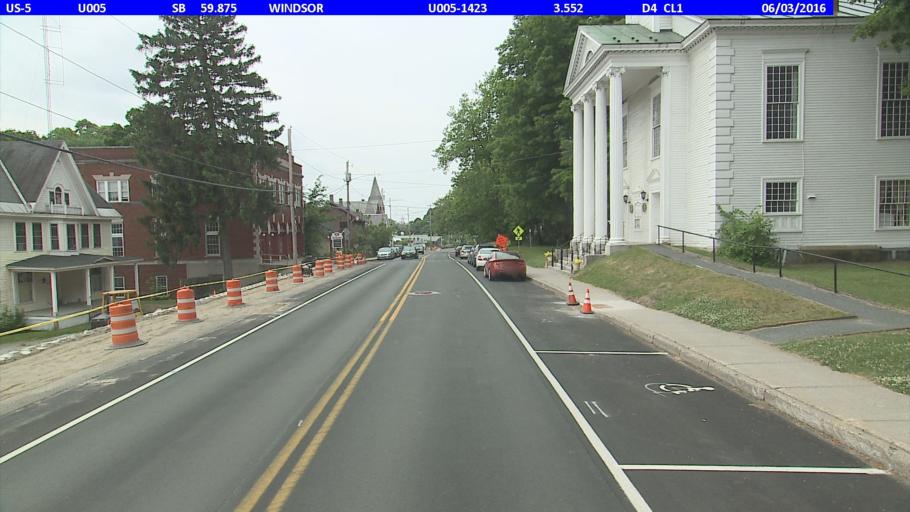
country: US
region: Vermont
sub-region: Windsor County
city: Windsor
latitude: 43.4782
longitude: -72.3874
